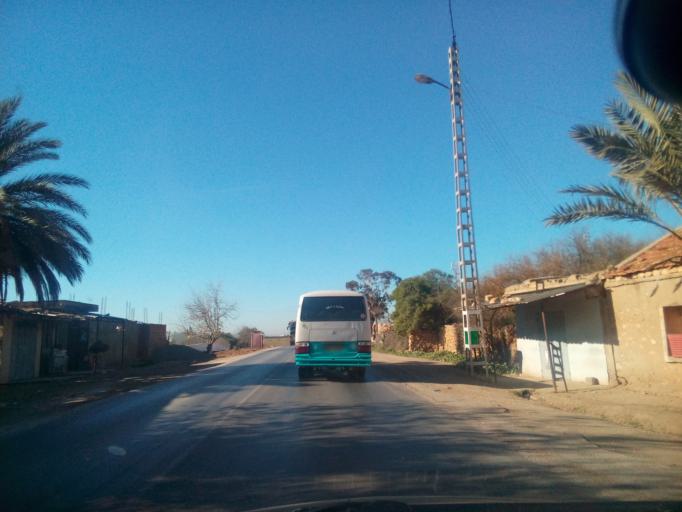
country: DZ
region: Relizane
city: Djidiouia
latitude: 35.8937
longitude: 0.7222
